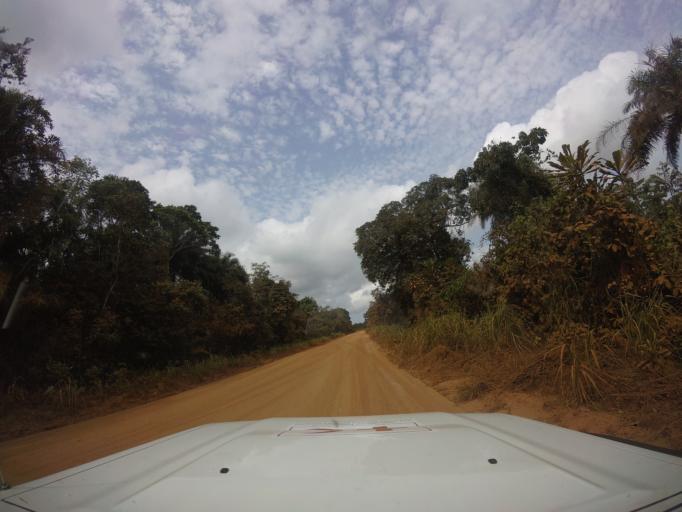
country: LR
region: Grand Cape Mount
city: Robertsport
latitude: 6.6816
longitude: -11.1322
